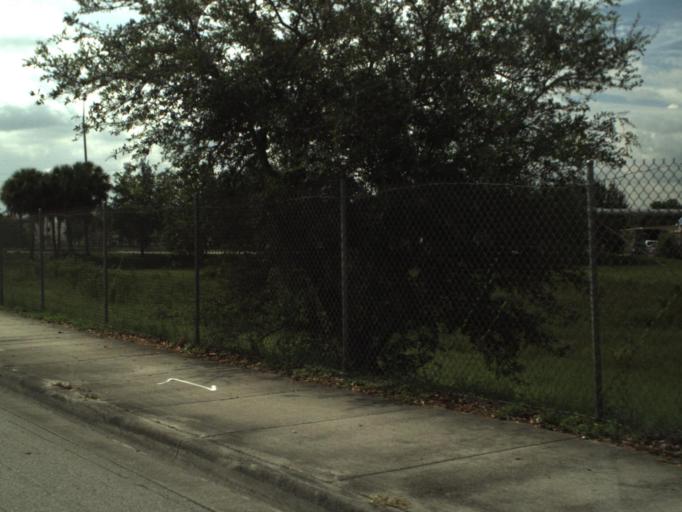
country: US
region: Florida
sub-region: Broward County
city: Davie
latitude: 26.0649
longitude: -80.2133
